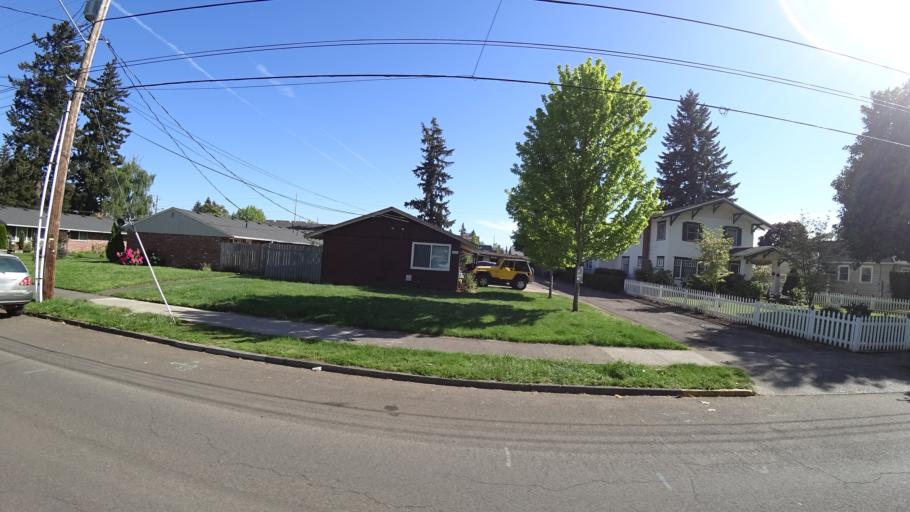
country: US
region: Oregon
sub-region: Washington County
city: Hillsboro
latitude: 45.5226
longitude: -122.9797
